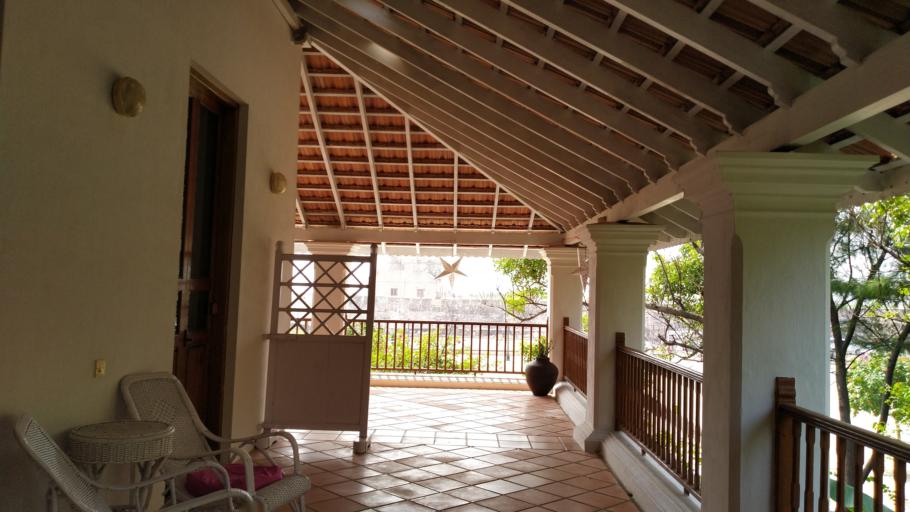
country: IN
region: Tamil Nadu
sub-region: Nagapattinam
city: Tharangambadi
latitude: 11.0259
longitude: 79.8560
